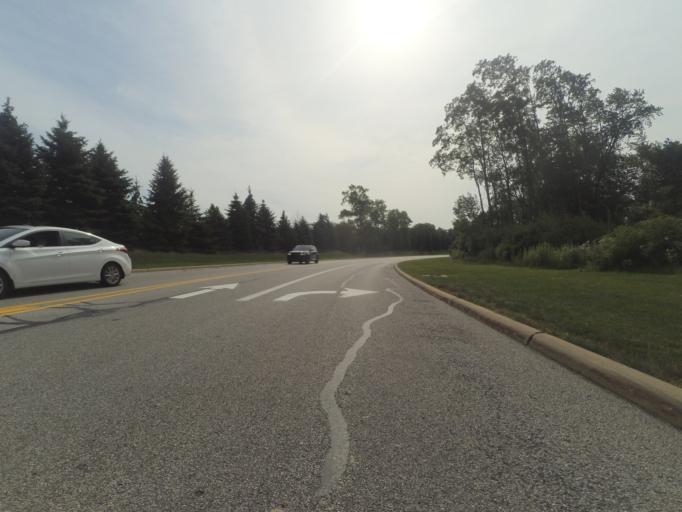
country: US
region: Ohio
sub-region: Cuyahoga County
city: Orange
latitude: 41.4653
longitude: -81.4852
